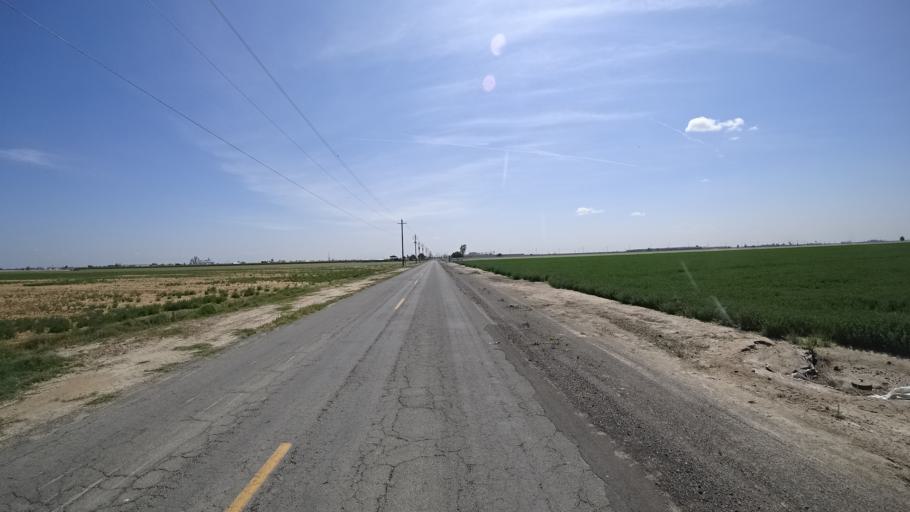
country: US
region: California
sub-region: Kings County
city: Home Garden
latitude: 36.2693
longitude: -119.6687
